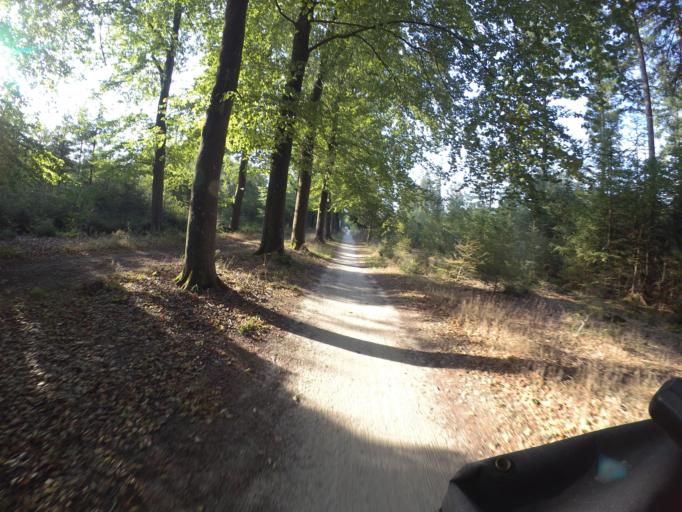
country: NL
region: Drenthe
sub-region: Gemeente Westerveld
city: Dwingeloo
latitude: 52.9299
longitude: 6.3320
